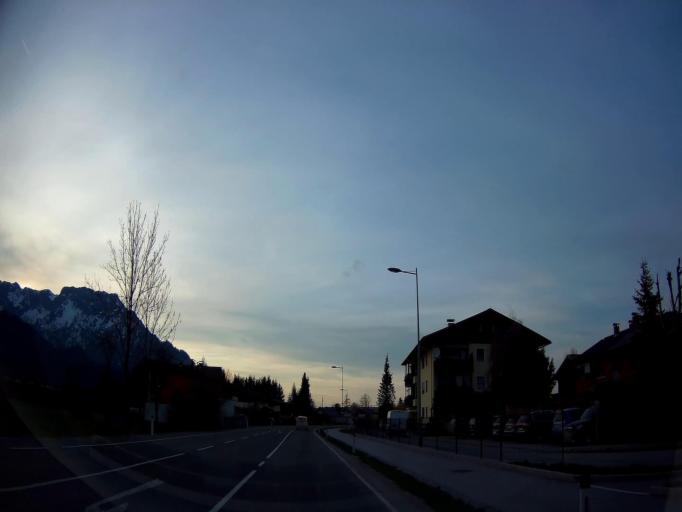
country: AT
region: Salzburg
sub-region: Politischer Bezirk Hallein
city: Puch bei Hallein
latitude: 47.7046
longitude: 13.0881
